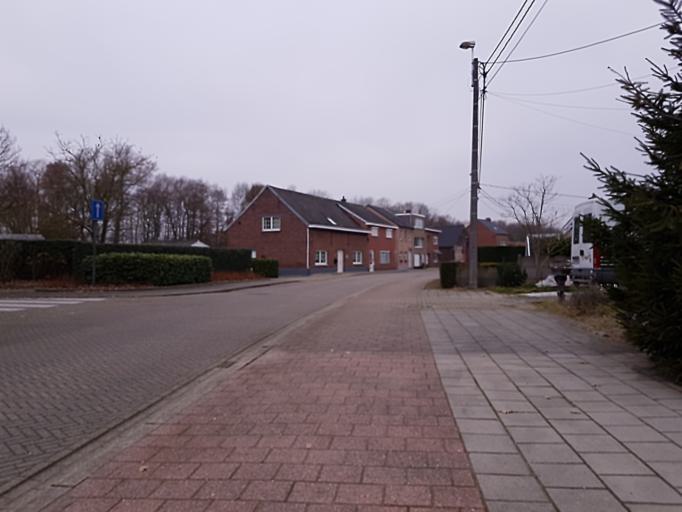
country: BE
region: Flanders
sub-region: Provincie Antwerpen
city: Rumst
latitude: 51.0678
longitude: 4.3962
